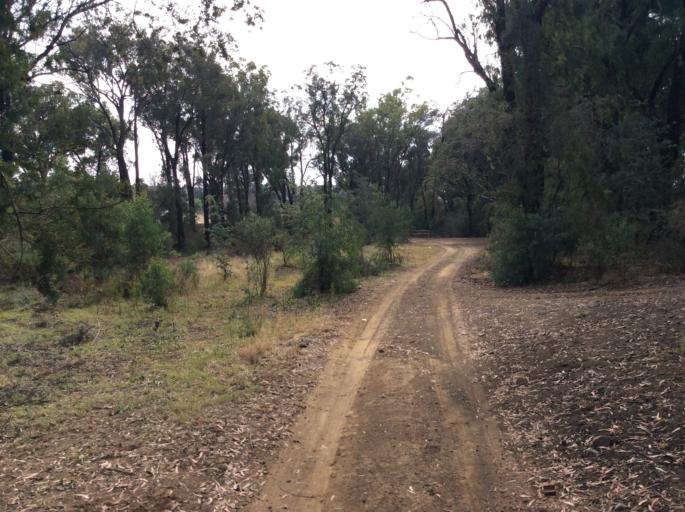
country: ZA
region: Orange Free State
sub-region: Xhariep District Municipality
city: Dewetsdorp
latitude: -29.5908
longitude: 26.6654
